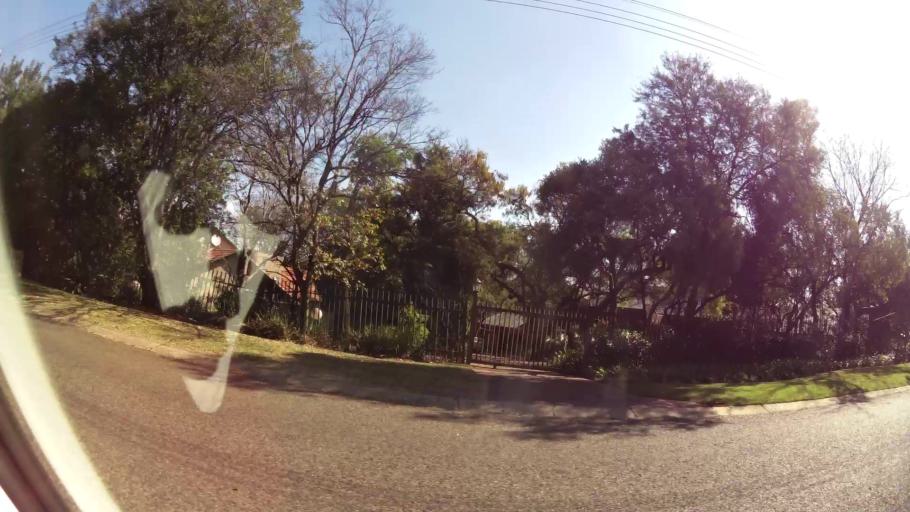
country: ZA
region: Gauteng
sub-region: City of Tshwane Metropolitan Municipality
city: Pretoria
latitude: -25.7579
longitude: 28.2656
